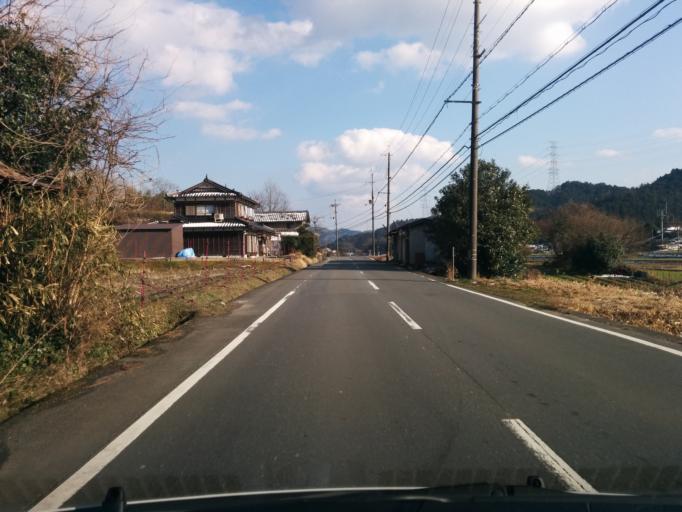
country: JP
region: Kyoto
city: Ayabe
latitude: 35.3675
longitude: 135.1965
